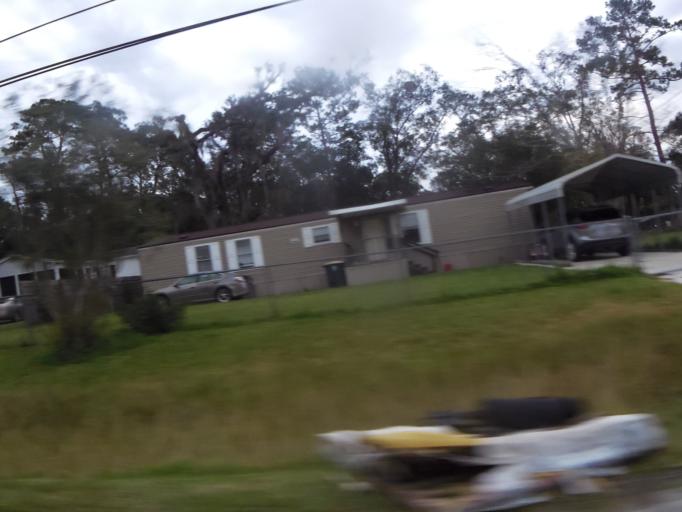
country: US
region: Florida
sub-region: Duval County
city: Jacksonville
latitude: 30.2615
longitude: -81.5814
